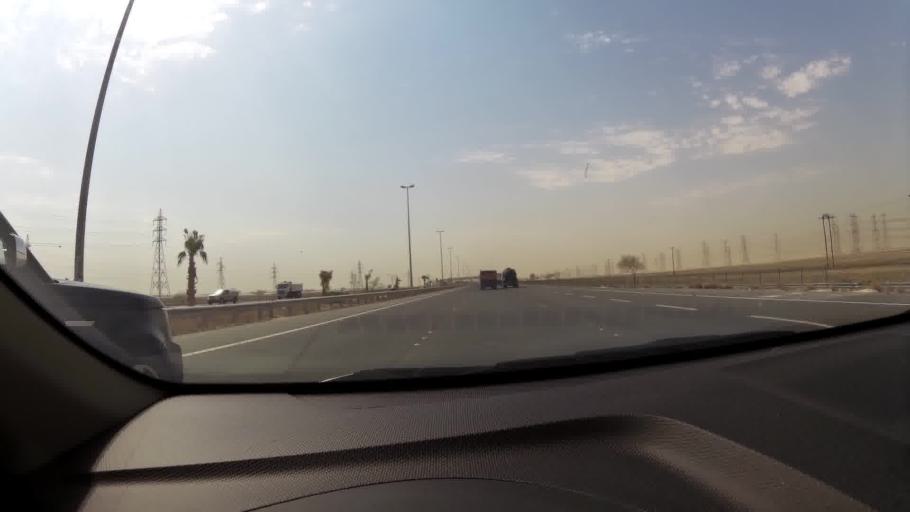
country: KW
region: Al Ahmadi
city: Al Fahahil
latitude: 28.8305
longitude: 48.2546
